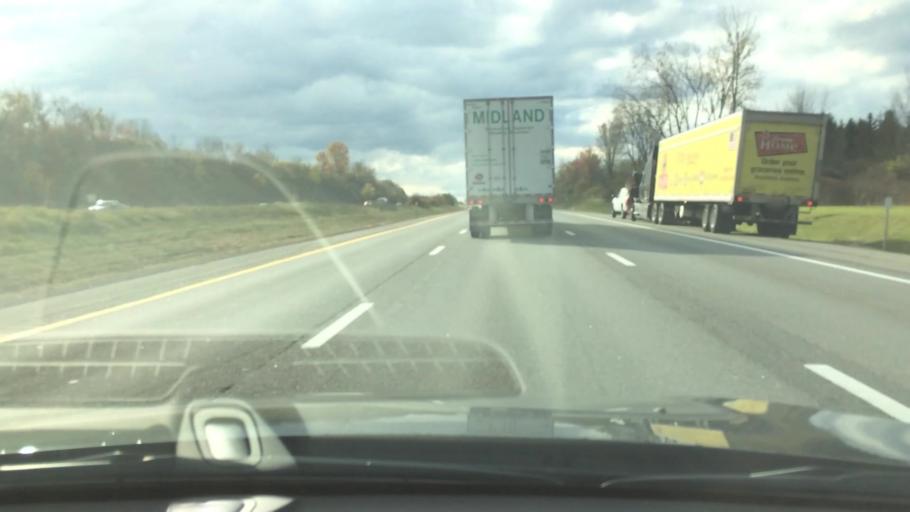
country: US
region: New York
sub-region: Saratoga County
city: Ballston Spa
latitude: 42.9906
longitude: -73.8039
